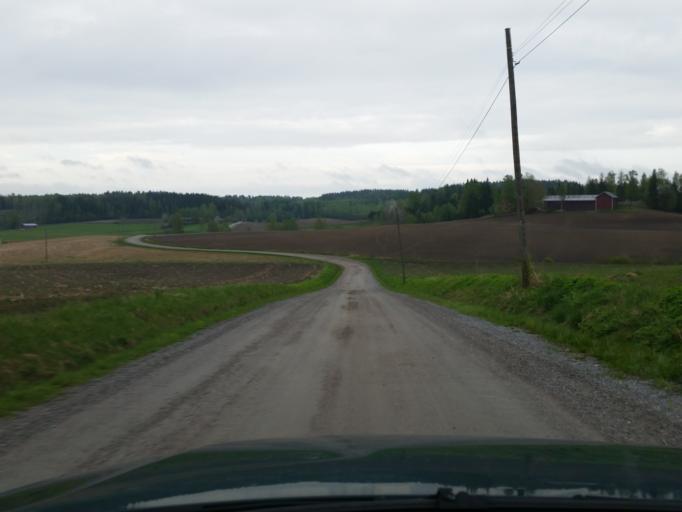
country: FI
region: Uusimaa
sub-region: Helsinki
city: Karjalohja
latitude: 60.1838
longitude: 23.6490
